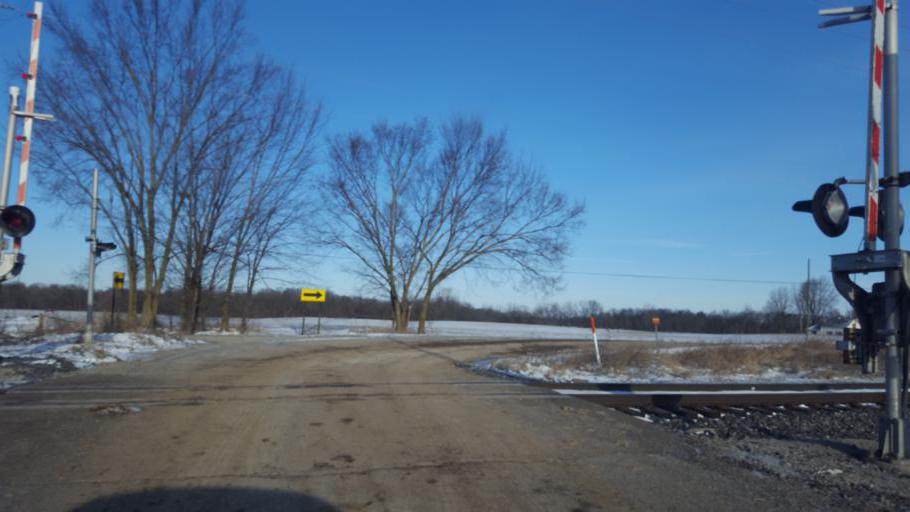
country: US
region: Ohio
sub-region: Morrow County
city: Mount Gilead
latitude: 40.6153
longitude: -82.8419
